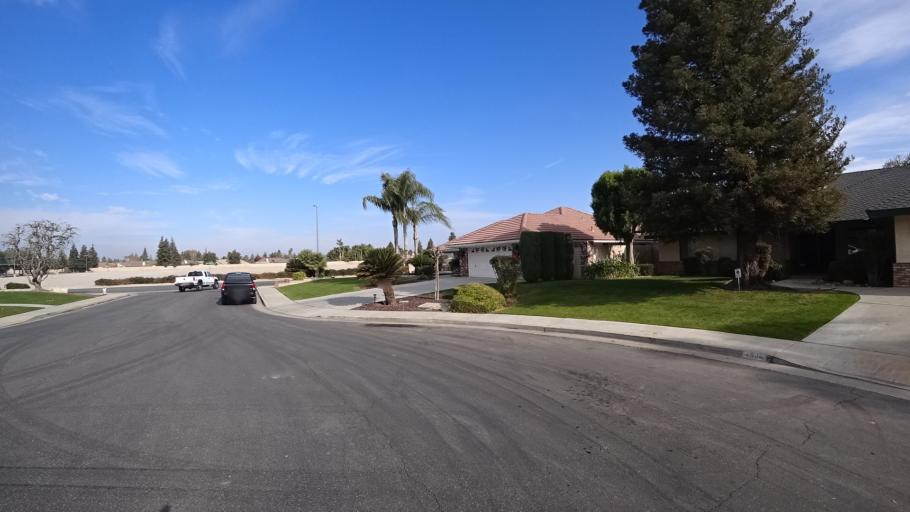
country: US
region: California
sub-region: Kern County
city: Greenacres
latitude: 35.4050
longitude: -119.0727
